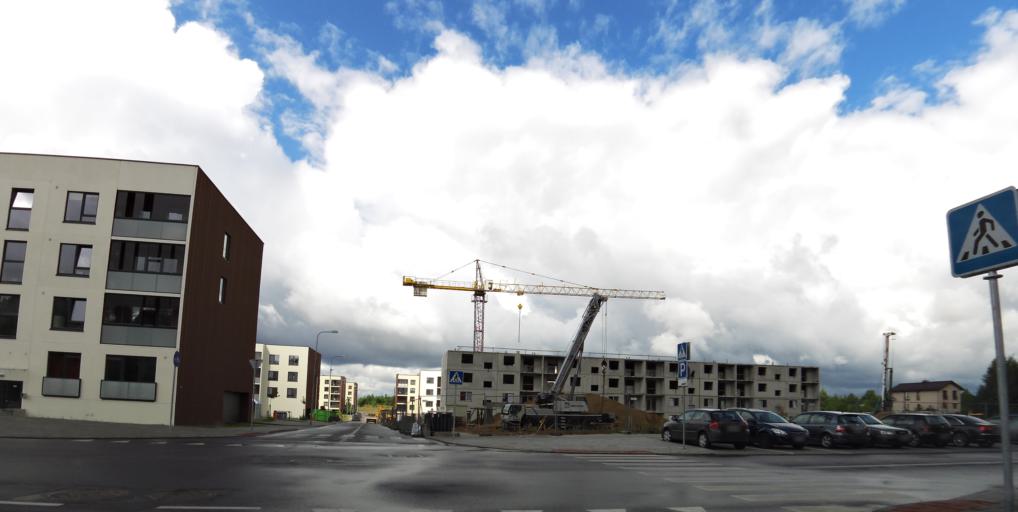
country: LT
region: Vilnius County
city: Pilaite
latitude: 54.7134
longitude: 25.1871
